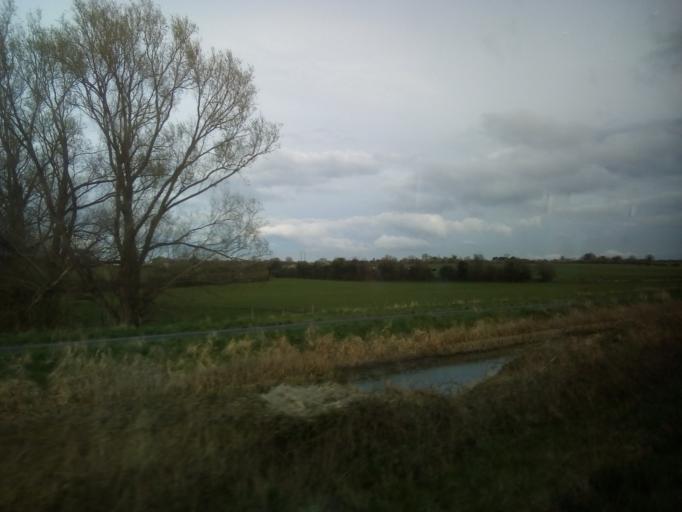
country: IE
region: Leinster
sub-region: Kildare
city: Kilcock
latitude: 53.4171
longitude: -6.7021
